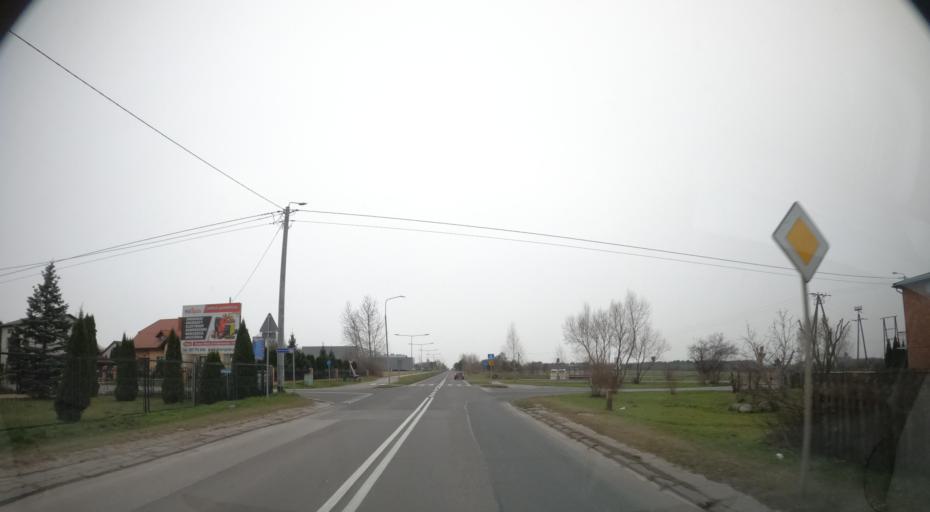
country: PL
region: Masovian Voivodeship
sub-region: Powiat radomski
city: Jastrzebia
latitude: 51.4497
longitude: 21.1936
